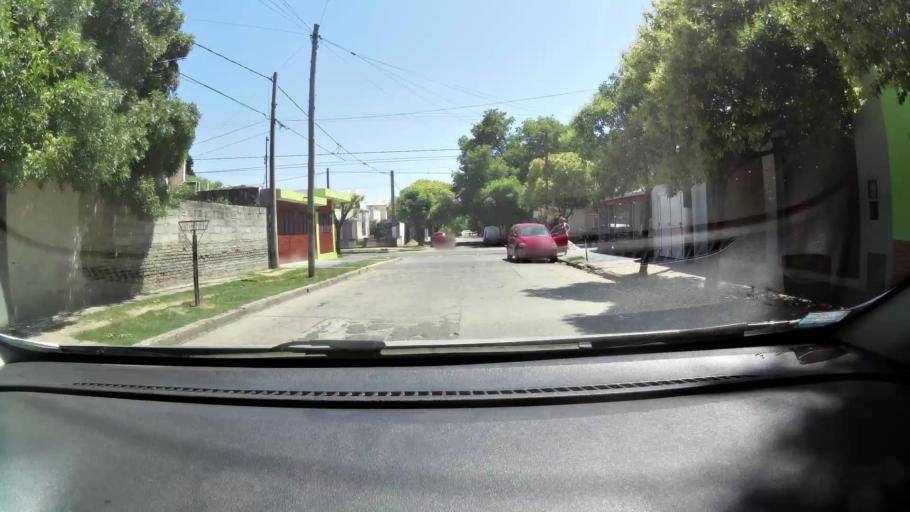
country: AR
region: Cordoba
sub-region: Departamento de Capital
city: Cordoba
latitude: -31.4321
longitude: -64.2036
